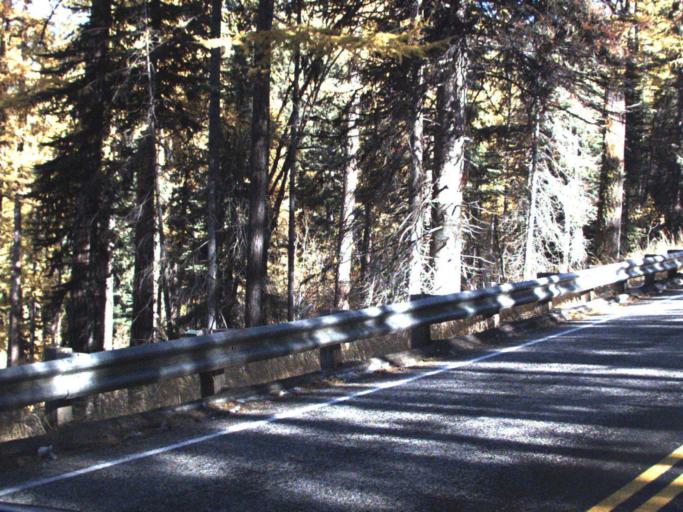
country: US
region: Washington
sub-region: Ferry County
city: Republic
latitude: 48.6034
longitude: -118.5021
